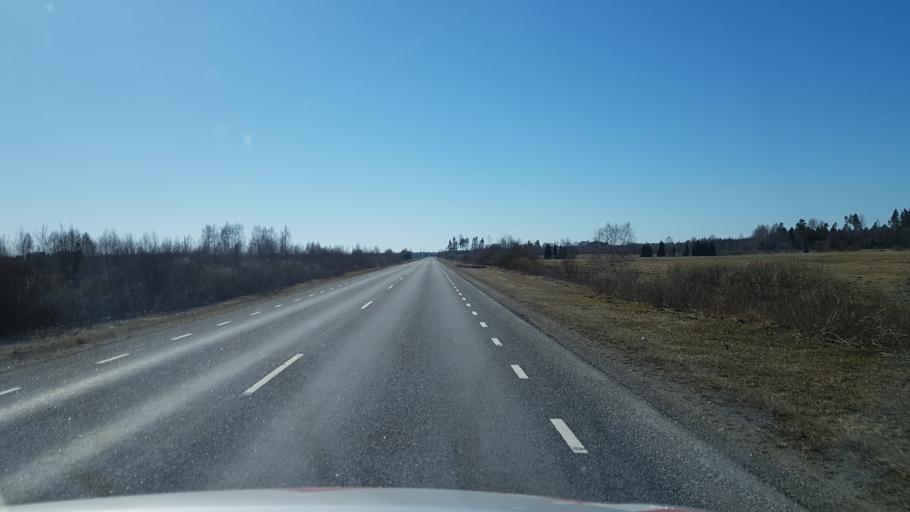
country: EE
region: Ida-Virumaa
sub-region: Aseri vald
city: Aseri
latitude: 59.3542
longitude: 26.7030
